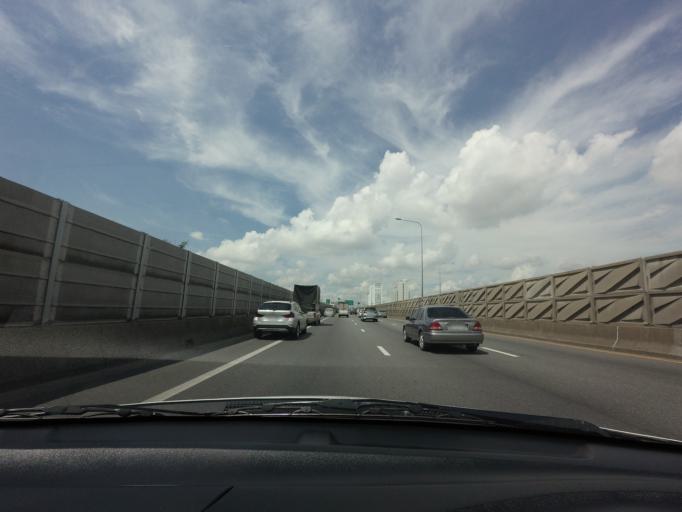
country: TH
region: Bangkok
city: Phaya Thai
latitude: 13.7873
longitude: 100.5366
